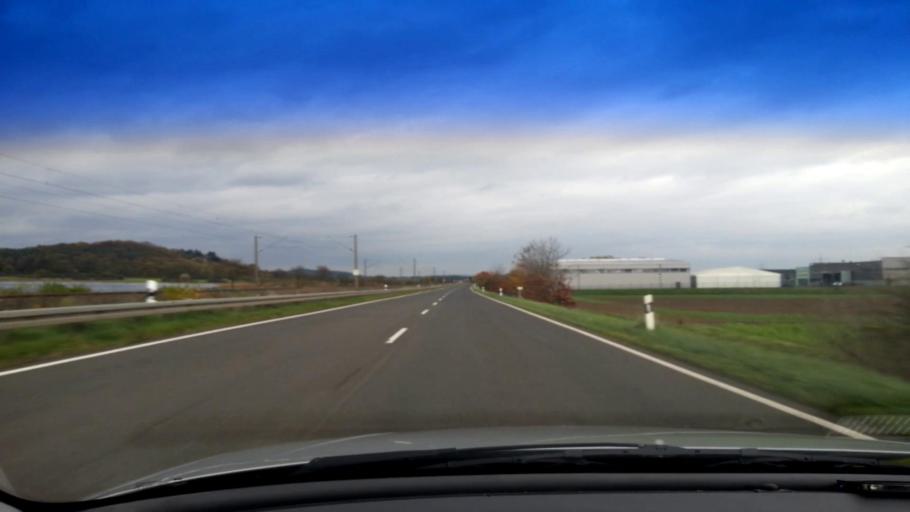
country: DE
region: Bavaria
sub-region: Upper Franconia
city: Viereth-Trunstadt
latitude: 49.9389
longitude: 10.7761
